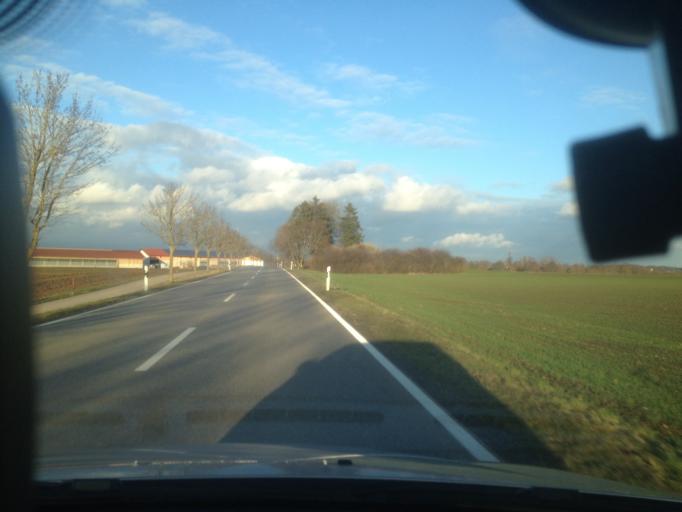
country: DE
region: Bavaria
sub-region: Swabia
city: Merching
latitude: 48.2534
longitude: 10.9715
